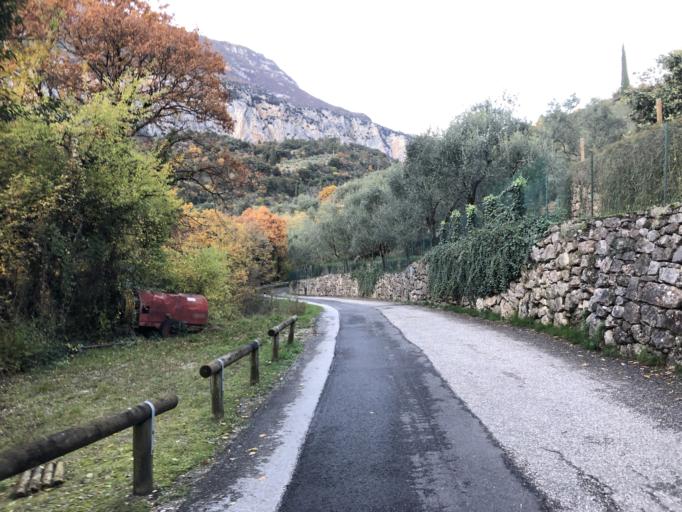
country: IT
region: Trentino-Alto Adige
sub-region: Provincia di Trento
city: Arco
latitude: 45.9319
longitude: 10.8854
